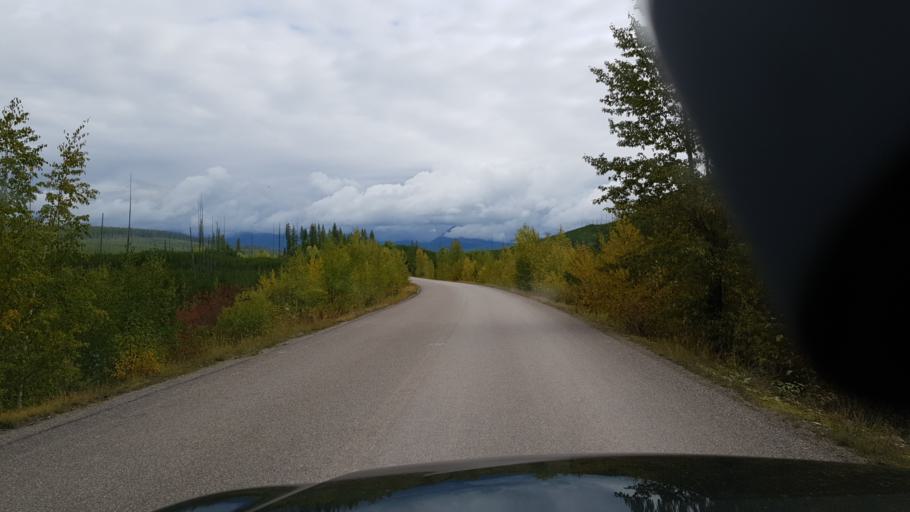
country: US
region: Montana
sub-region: Flathead County
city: Columbia Falls
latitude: 48.6211
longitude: -114.1370
